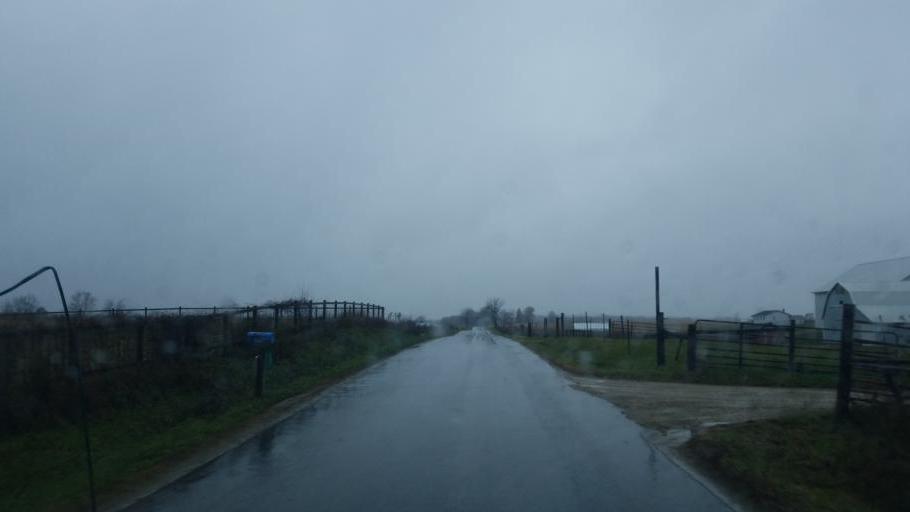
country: US
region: Indiana
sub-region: Adams County
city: Geneva
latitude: 40.6148
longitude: -84.9228
